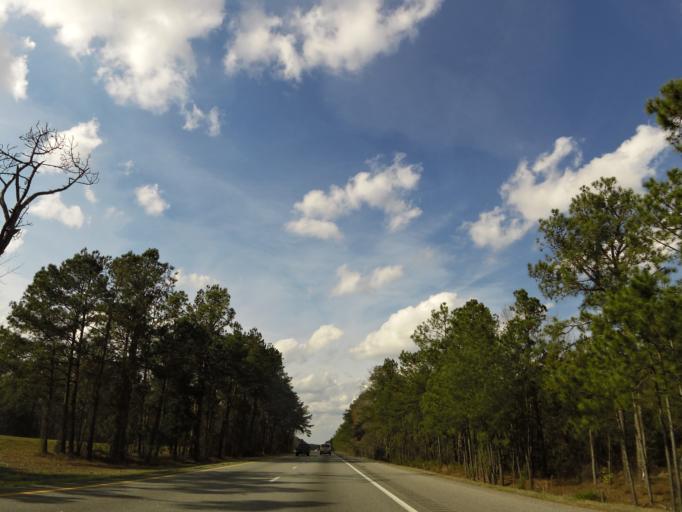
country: US
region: South Carolina
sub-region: Dorchester County
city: Ridgeville
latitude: 33.1733
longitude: -80.3680
